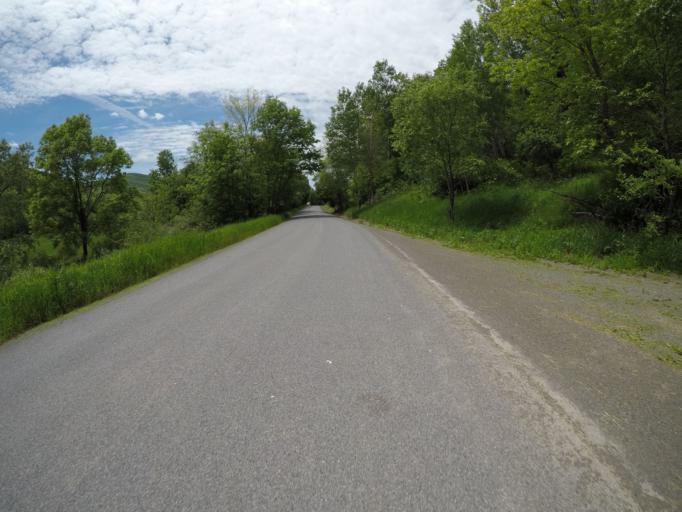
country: US
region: New York
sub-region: Delaware County
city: Stamford
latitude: 42.2574
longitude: -74.5255
